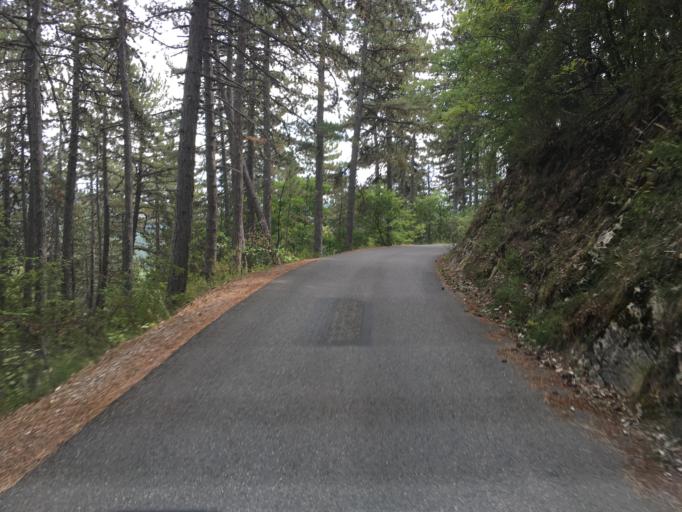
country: FR
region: Provence-Alpes-Cote d'Azur
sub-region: Departement des Alpes-de-Haute-Provence
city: Digne-les-Bains
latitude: 44.2100
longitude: 6.1504
